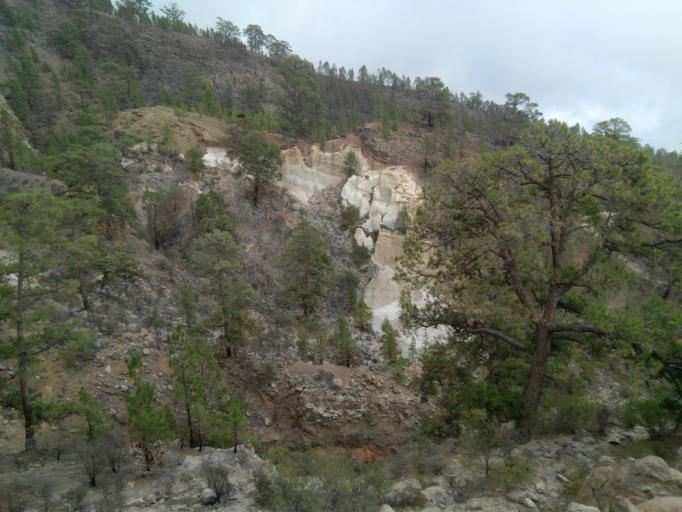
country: ES
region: Canary Islands
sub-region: Provincia de Santa Cruz de Tenerife
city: Vilaflor
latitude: 28.1901
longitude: -16.6048
